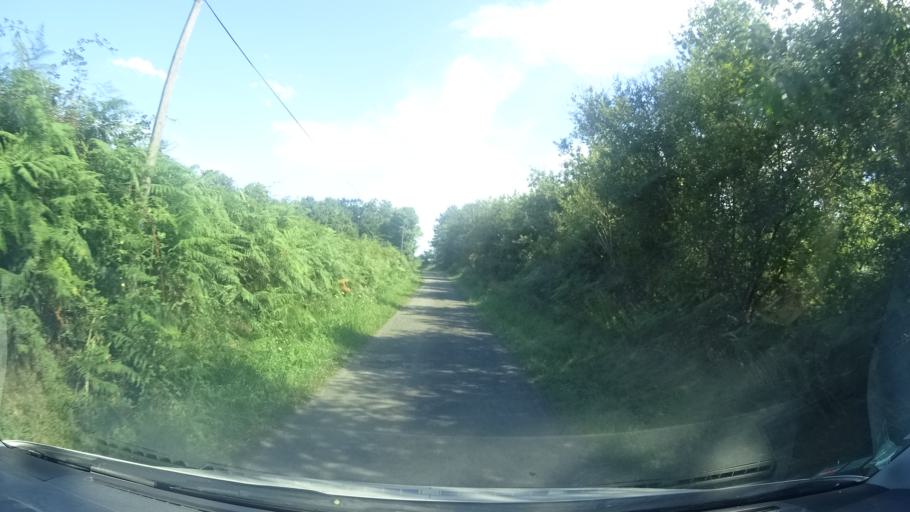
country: FR
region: Aquitaine
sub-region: Departement des Pyrenees-Atlantiques
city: Mont
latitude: 43.4958
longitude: -0.6683
